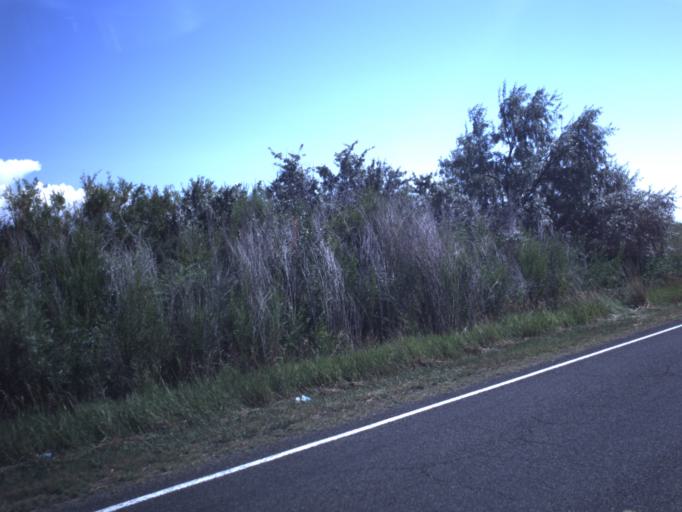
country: US
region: Utah
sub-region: Duchesne County
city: Roosevelt
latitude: 40.2579
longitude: -110.2022
